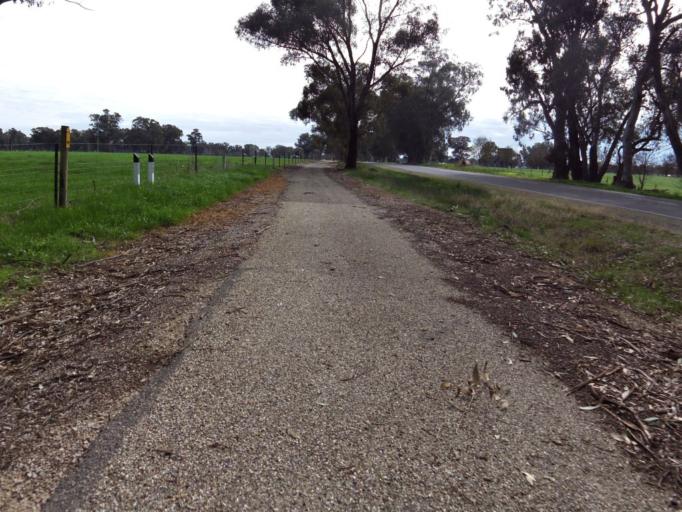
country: AU
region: Victoria
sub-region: Wangaratta
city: Wangaratta
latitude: -36.4296
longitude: 146.3580
